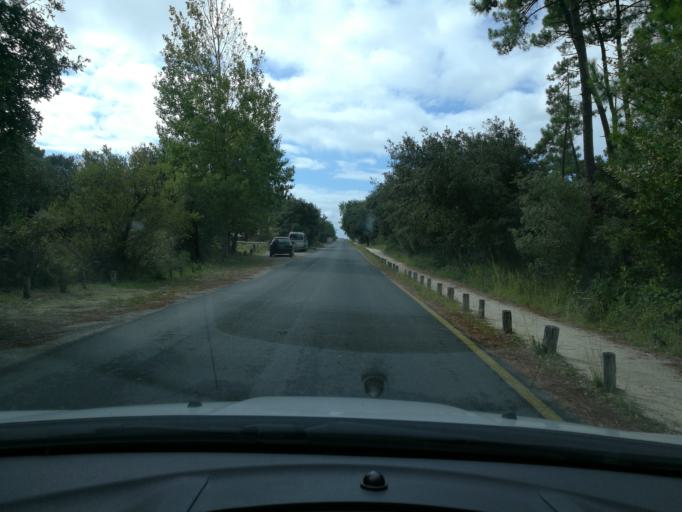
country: FR
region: Poitou-Charentes
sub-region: Departement de la Charente-Maritime
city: Saint-Trojan-les-Bains
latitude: 45.8567
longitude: -1.2441
